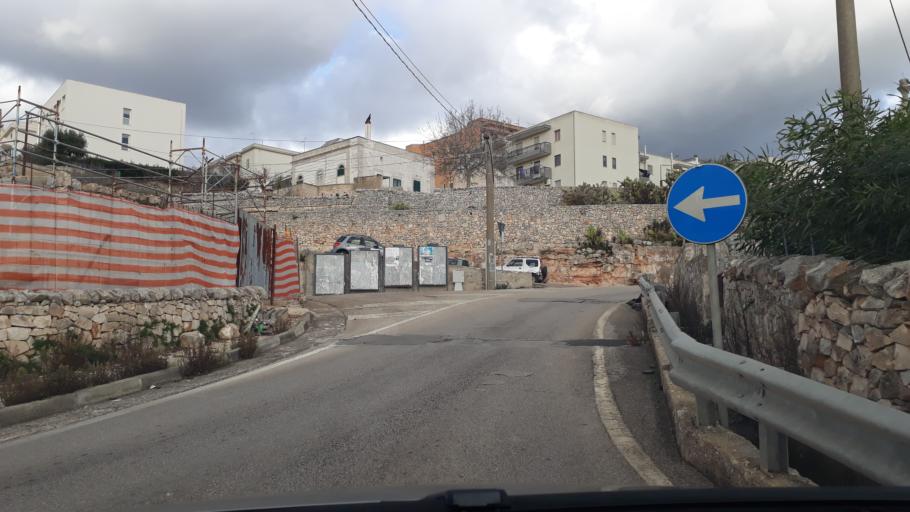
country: IT
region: Apulia
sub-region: Provincia di Brindisi
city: Cisternino
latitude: 40.7386
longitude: 17.4294
